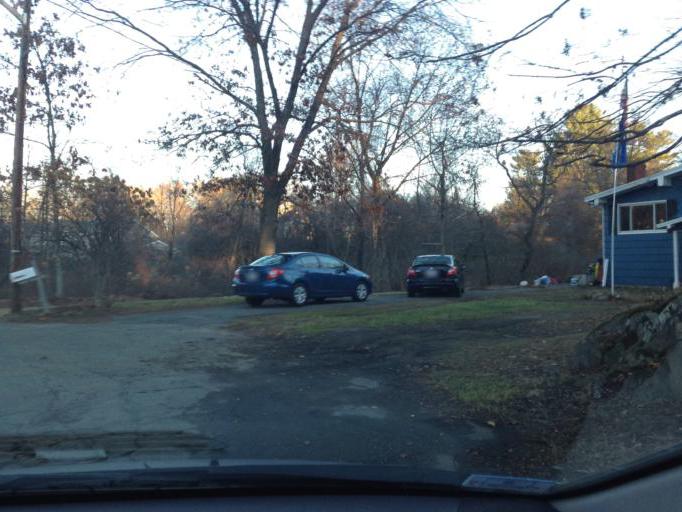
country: US
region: Massachusetts
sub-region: Middlesex County
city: Concord
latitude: 42.4779
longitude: -71.3183
